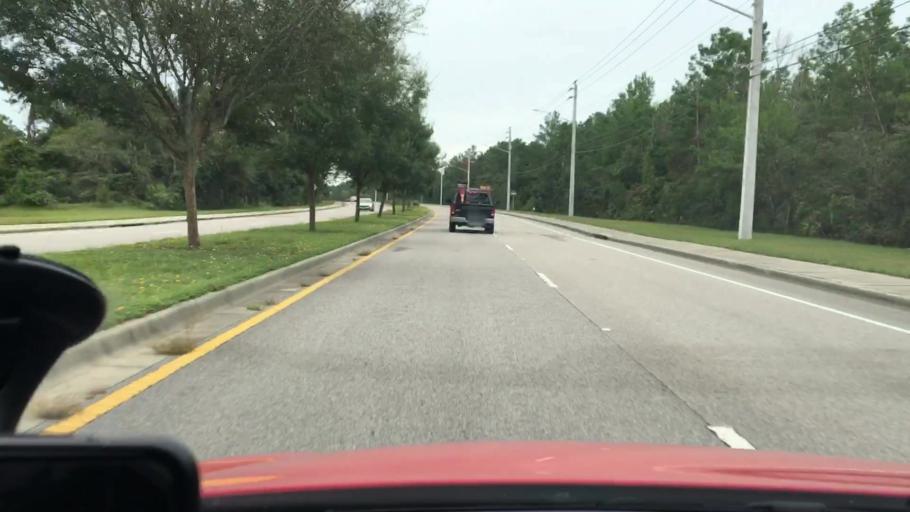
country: US
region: Florida
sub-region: Flagler County
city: Flagler Beach
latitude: 29.4917
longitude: -81.1881
